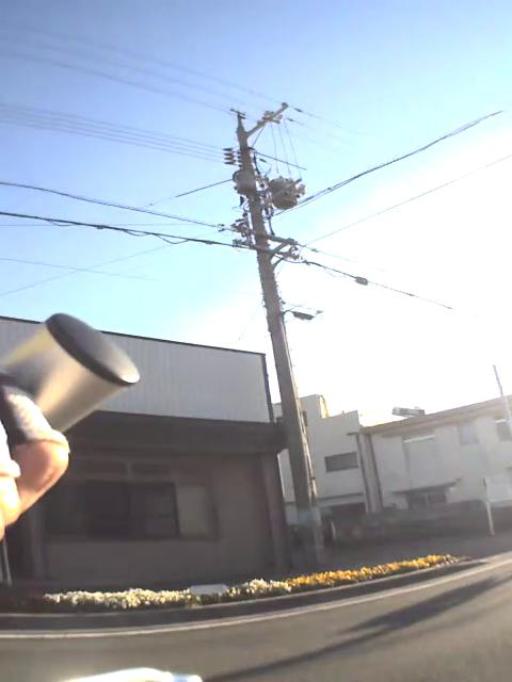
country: JP
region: Yamaguchi
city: Nagato
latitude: 34.3883
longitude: 131.1991
